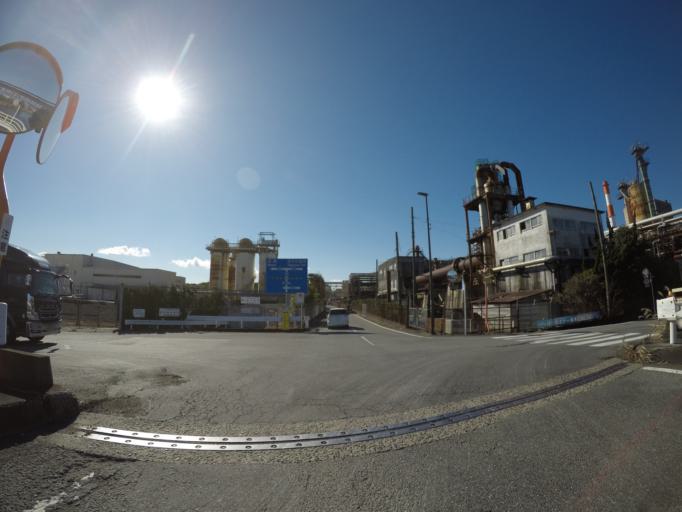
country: JP
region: Shizuoka
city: Fuji
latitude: 35.1443
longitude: 138.7123
